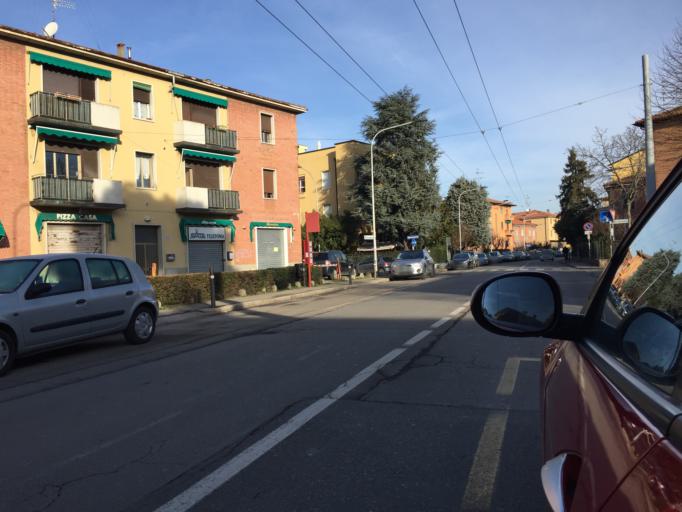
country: IT
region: Emilia-Romagna
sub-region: Provincia di Bologna
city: Casalecchio di Reno
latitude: 44.4978
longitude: 11.2953
